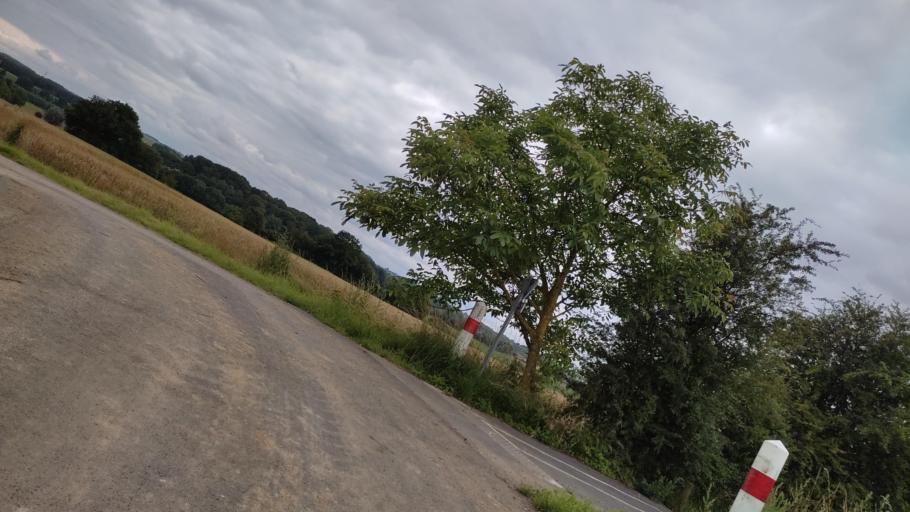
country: FR
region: Nord-Pas-de-Calais
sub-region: Departement du Pas-de-Calais
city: Beaumetz-les-Loges
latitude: 50.2312
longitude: 2.6359
